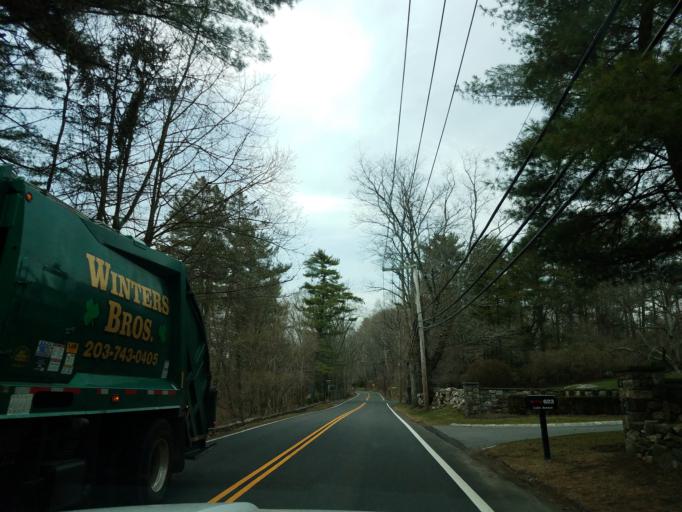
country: US
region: Connecticut
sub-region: Fairfield County
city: Glenville
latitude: 41.0679
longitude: -73.6394
